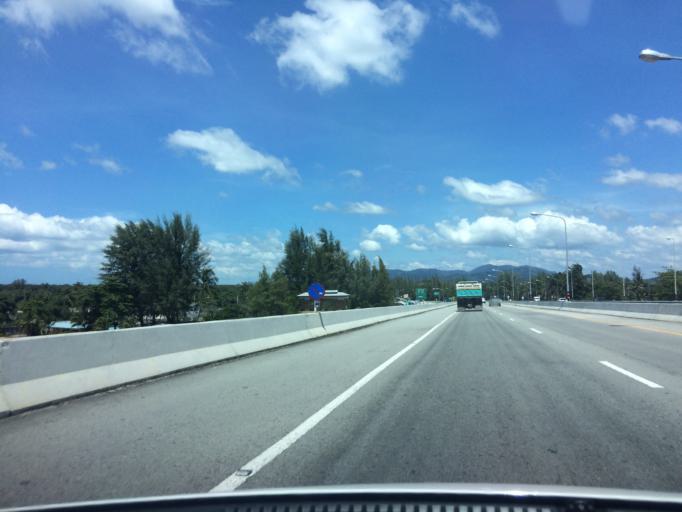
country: TH
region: Phuket
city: Thalang
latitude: 8.2027
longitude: 98.2985
